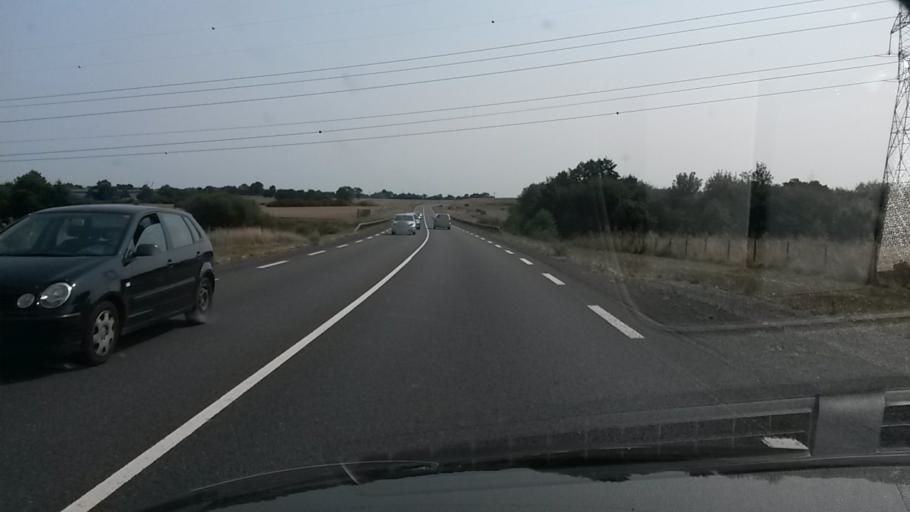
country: FR
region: Pays de la Loire
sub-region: Departement de la Loire-Atlantique
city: Mesanger
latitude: 47.4241
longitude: -1.1868
